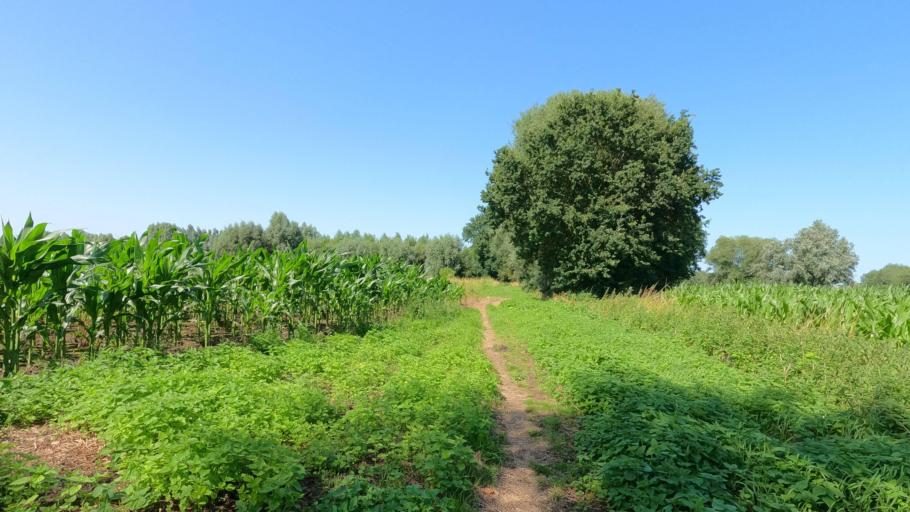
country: BE
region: Flanders
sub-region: Provincie Vlaams-Brabant
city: Kapelle-op-den-Bos
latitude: 51.0319
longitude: 4.3456
